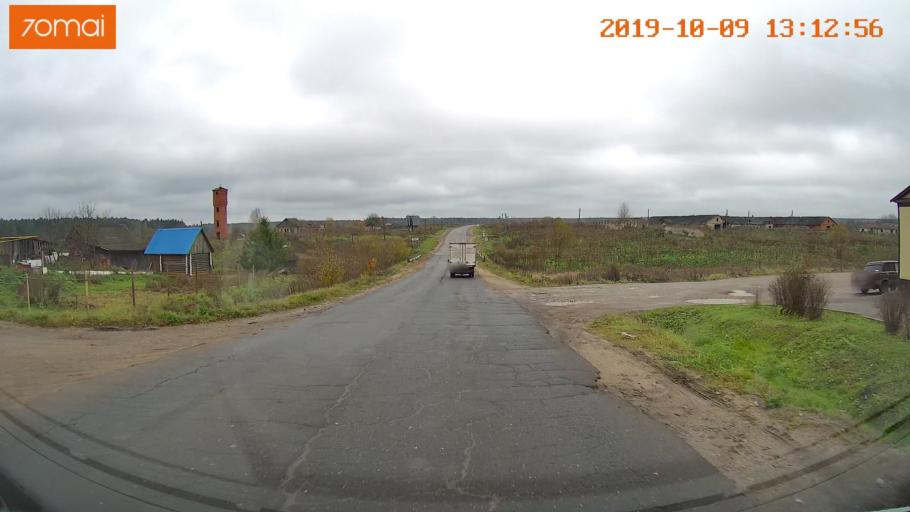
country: RU
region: Jaroslavl
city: Lyubim
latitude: 58.3633
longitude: 40.7079
